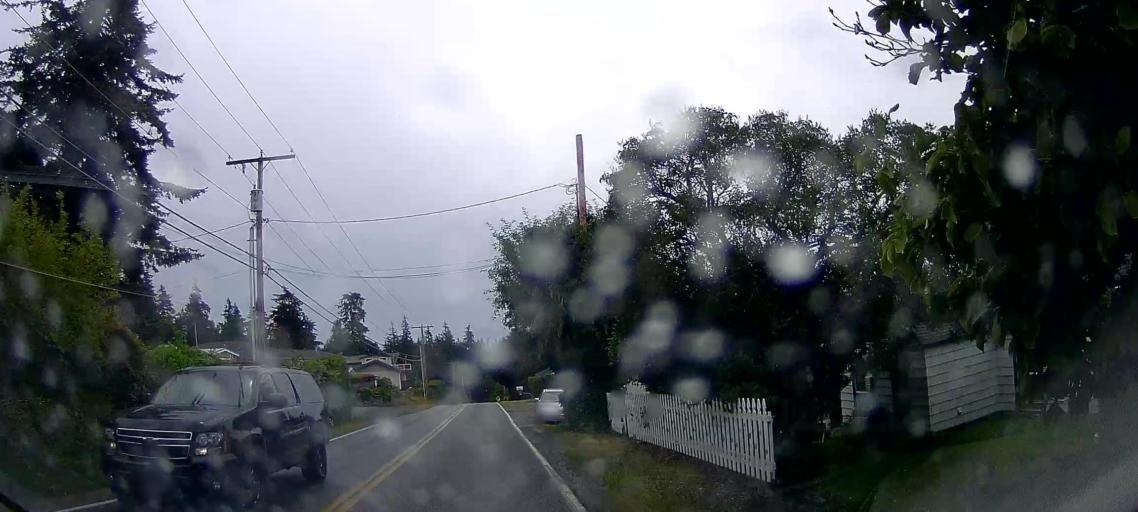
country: US
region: Washington
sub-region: Whatcom County
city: Birch Bay
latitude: 48.8180
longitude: -122.7065
